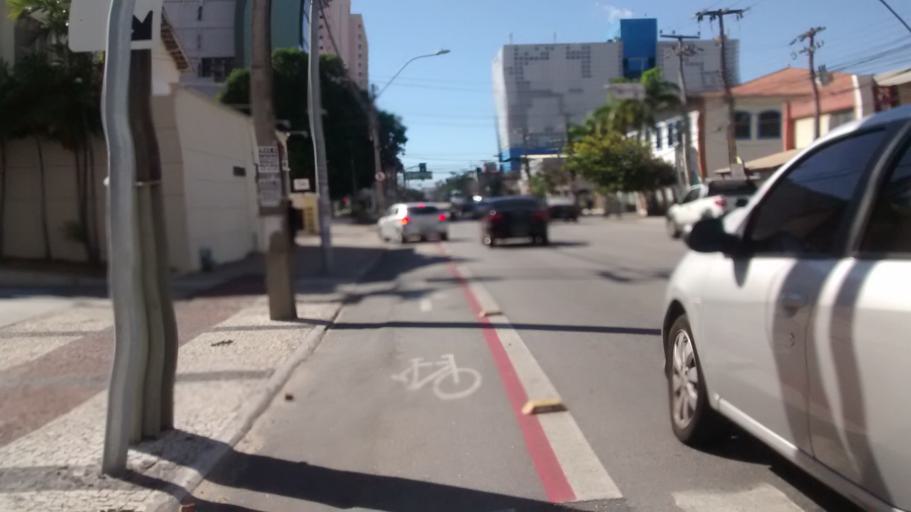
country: BR
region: Ceara
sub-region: Fortaleza
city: Fortaleza
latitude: -3.7358
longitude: -38.4993
